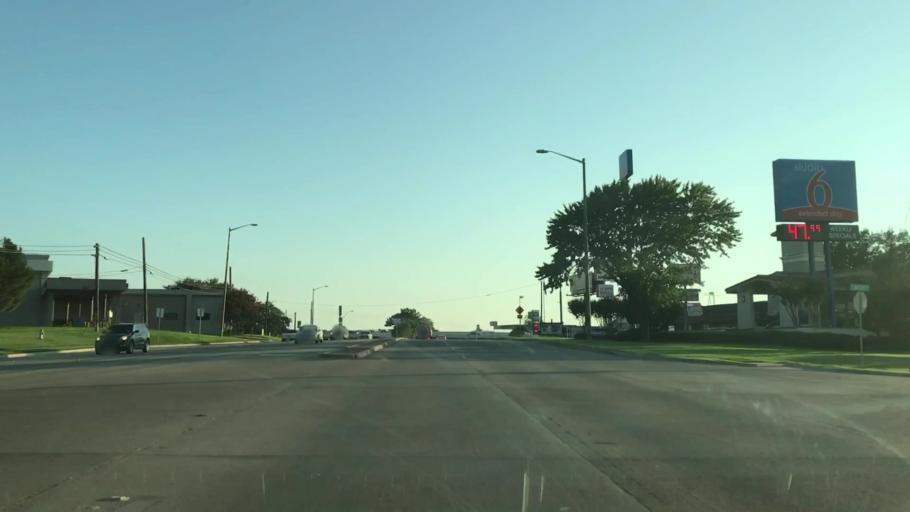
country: US
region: Texas
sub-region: Denton County
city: Denton
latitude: 33.1989
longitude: -97.1381
